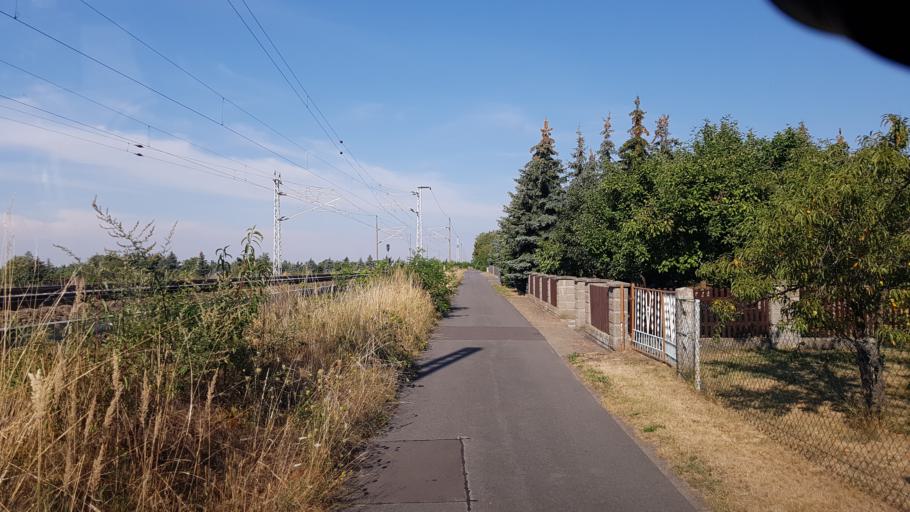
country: DE
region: Brandenburg
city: Plessa
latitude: 51.4707
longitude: 13.6031
